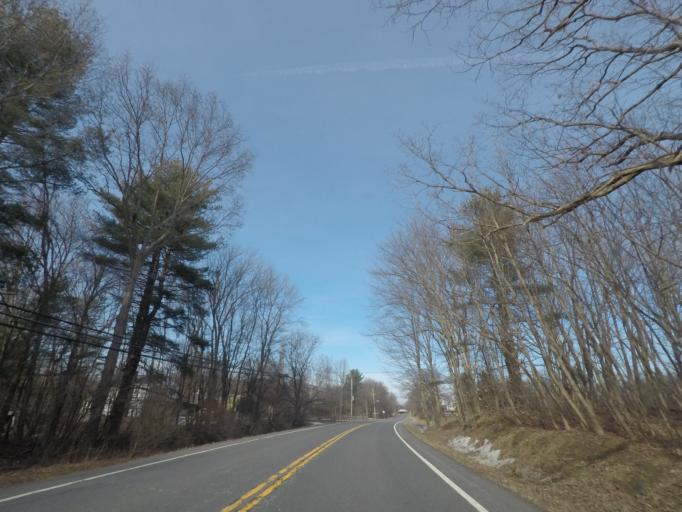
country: US
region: New York
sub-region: Rensselaer County
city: Nassau
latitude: 42.4931
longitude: -73.6244
